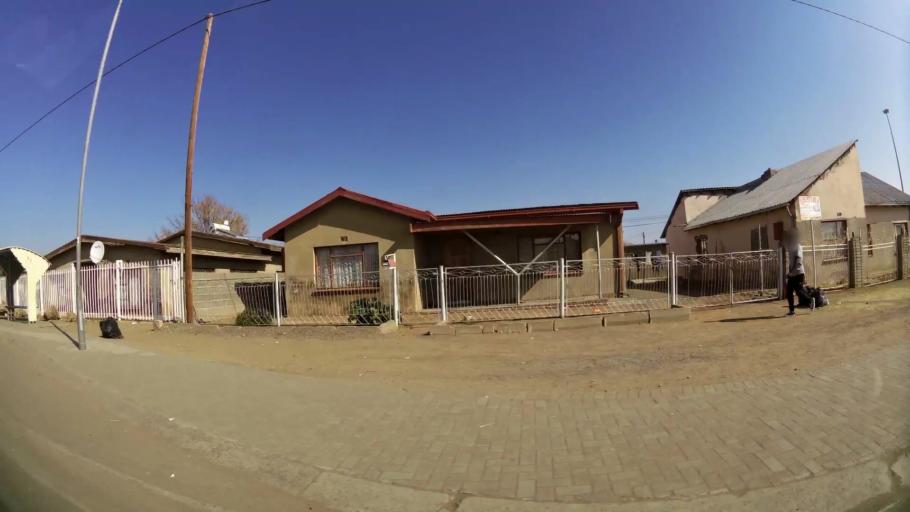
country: ZA
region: Orange Free State
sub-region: Mangaung Metropolitan Municipality
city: Bloemfontein
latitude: -29.1512
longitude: 26.2403
